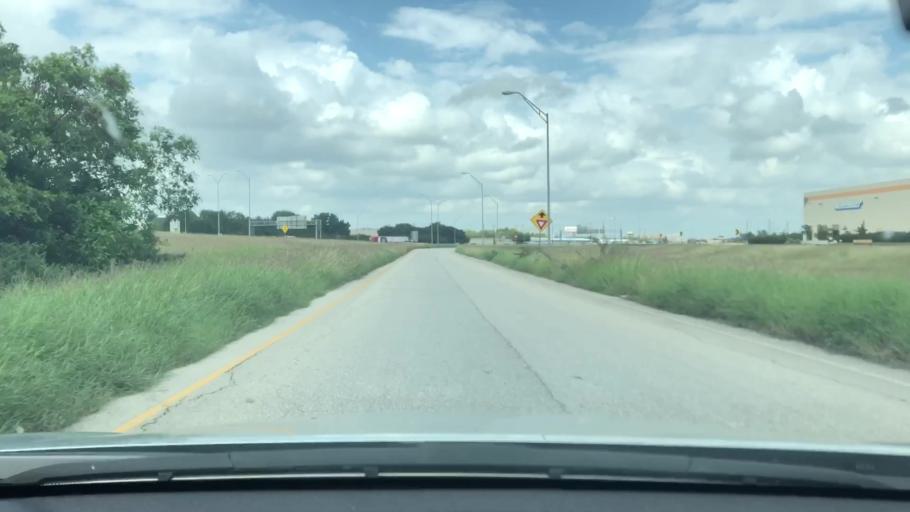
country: US
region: Texas
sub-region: Bexar County
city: Kirby
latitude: 29.4376
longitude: -98.3892
